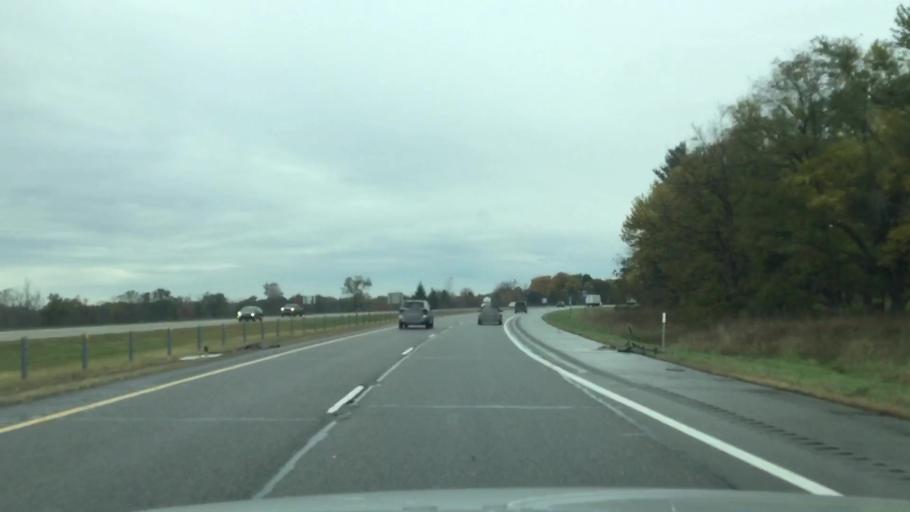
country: US
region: Michigan
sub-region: Calhoun County
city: Albion
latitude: 42.2643
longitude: -84.7668
